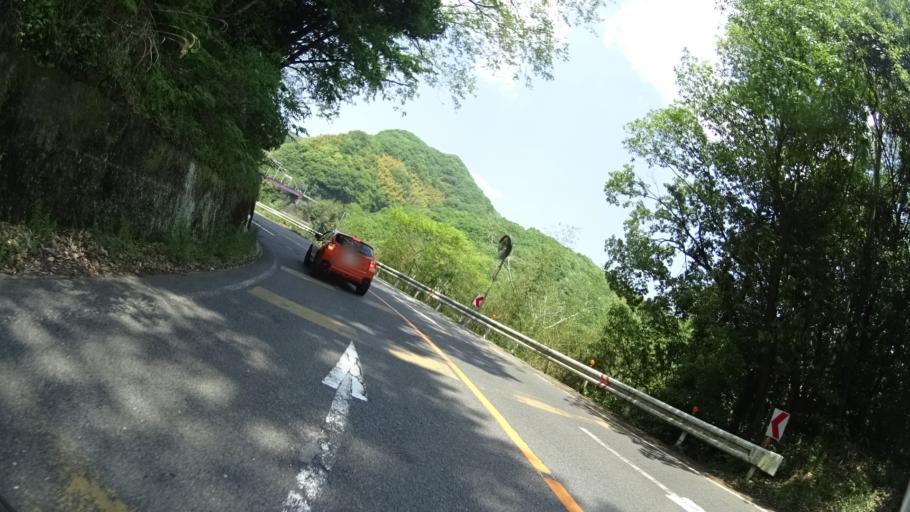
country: JP
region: Ehime
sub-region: Shikoku-chuo Shi
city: Matsuyama
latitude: 33.8873
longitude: 132.8368
